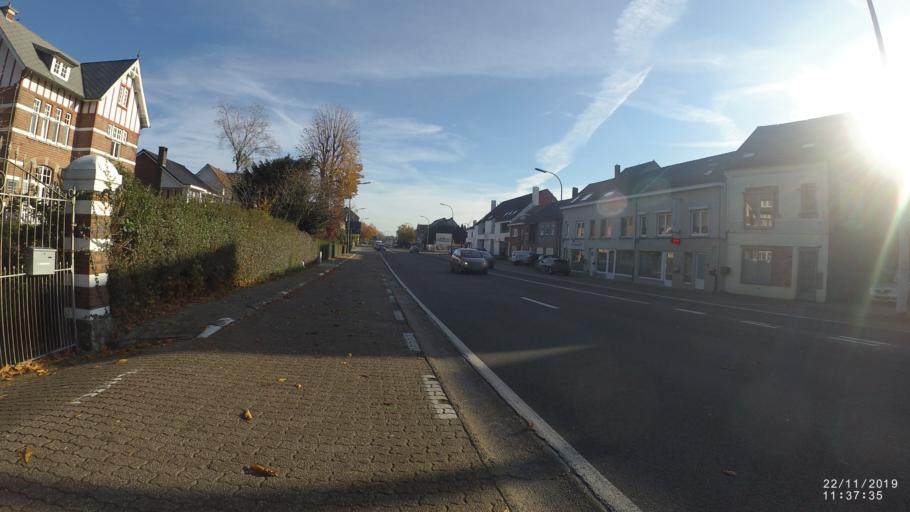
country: BE
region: Flanders
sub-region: Provincie Limburg
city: Hasselt
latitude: 50.9438
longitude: 5.3444
